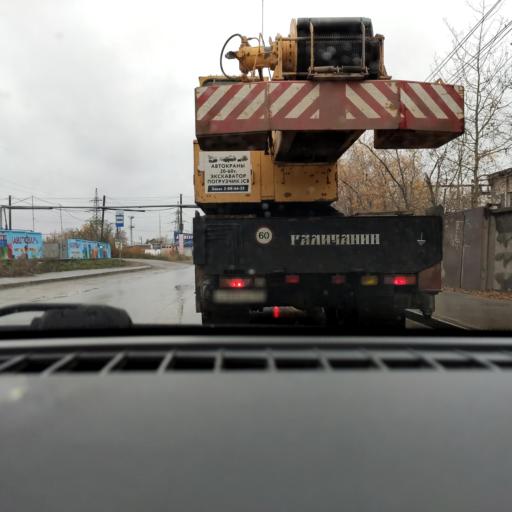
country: RU
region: Perm
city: Froly
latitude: 57.9528
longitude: 56.2572
